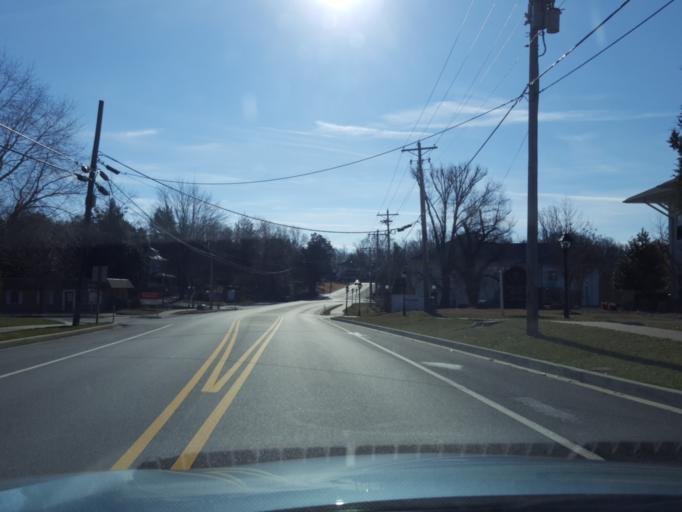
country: US
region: Maryland
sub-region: Calvert County
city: Prince Frederick
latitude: 38.5377
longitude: -76.5812
